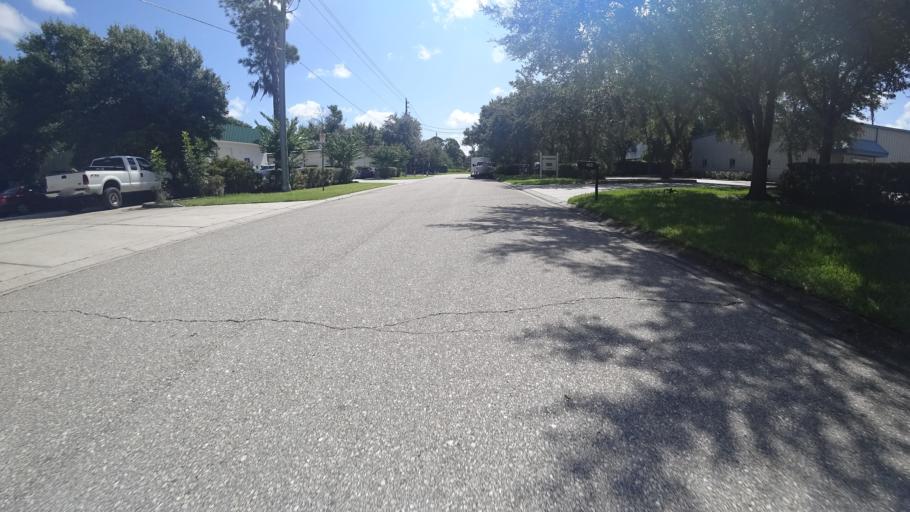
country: US
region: Florida
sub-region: Manatee County
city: Samoset
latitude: 27.4387
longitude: -82.5353
